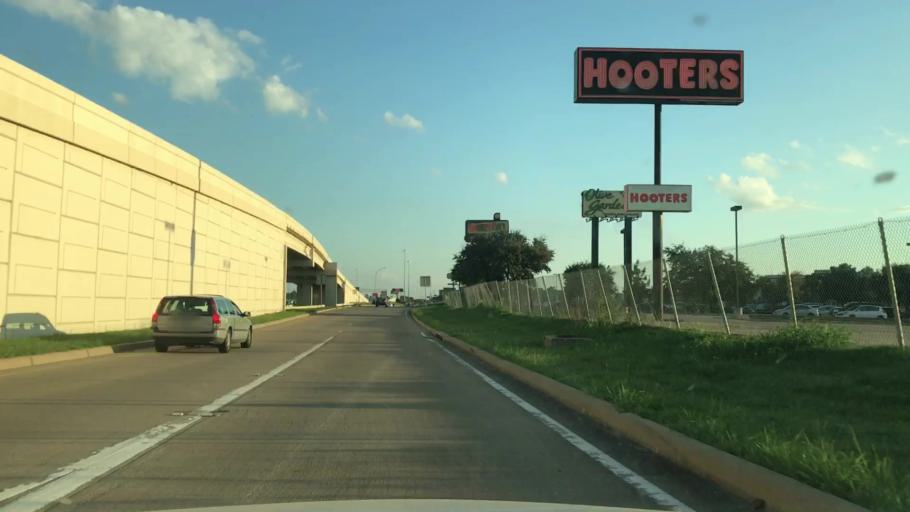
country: US
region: Texas
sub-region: Dallas County
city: Mesquite
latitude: 32.8180
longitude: -96.6293
